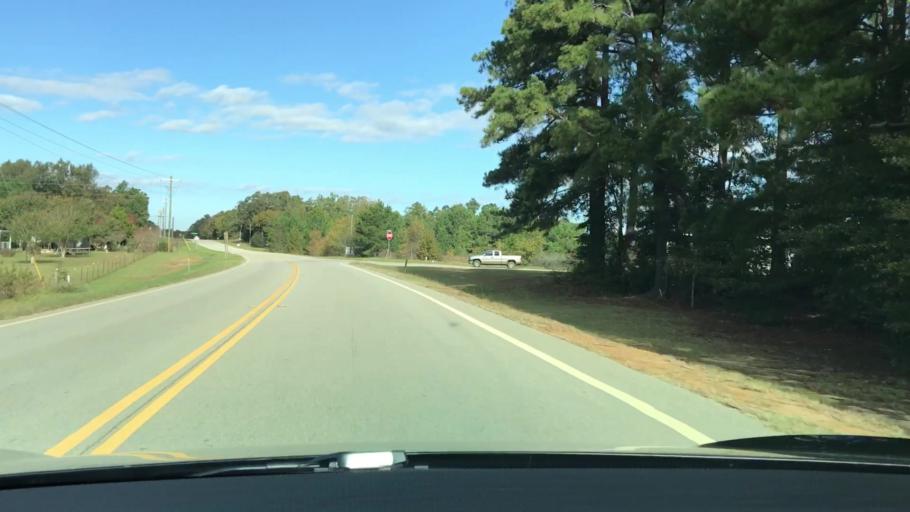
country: US
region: Georgia
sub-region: Jefferson County
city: Wrens
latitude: 33.1875
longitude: -82.4555
